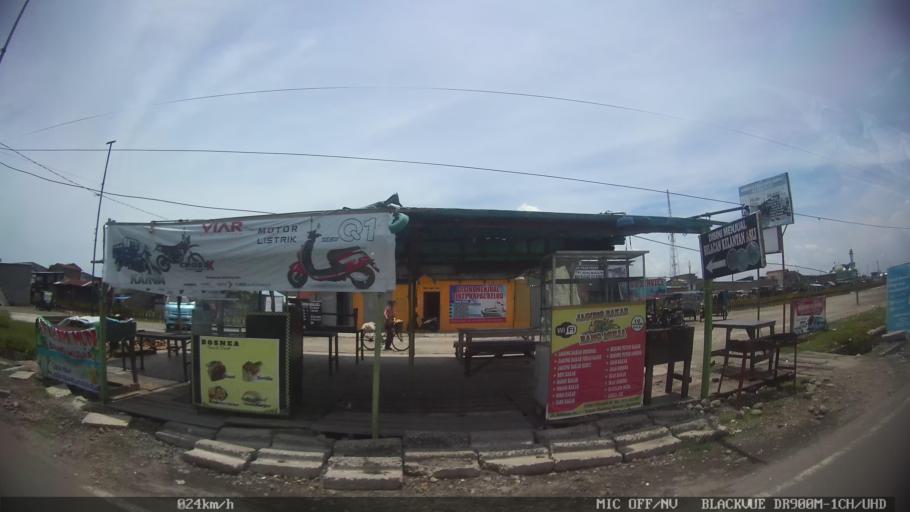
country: ID
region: North Sumatra
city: Belawan
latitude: 3.7816
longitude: 98.6822
